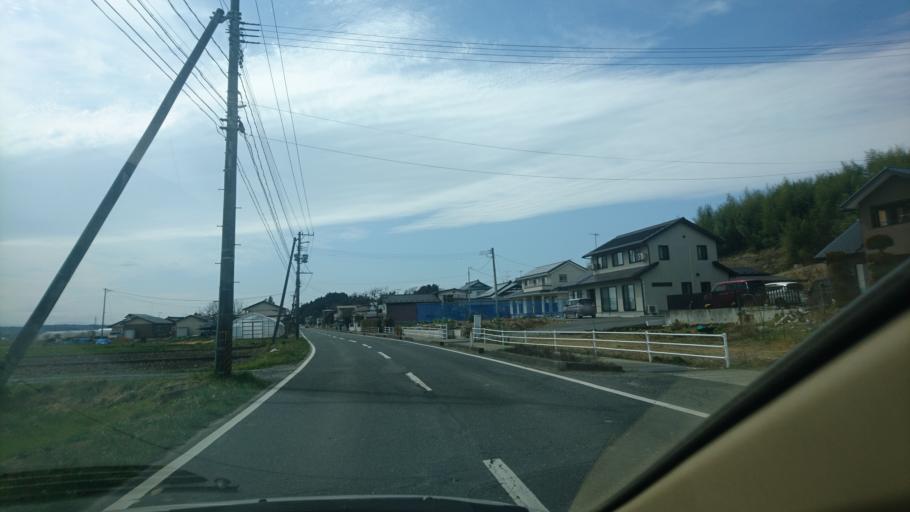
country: JP
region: Miyagi
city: Furukawa
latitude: 38.7501
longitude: 141.0067
